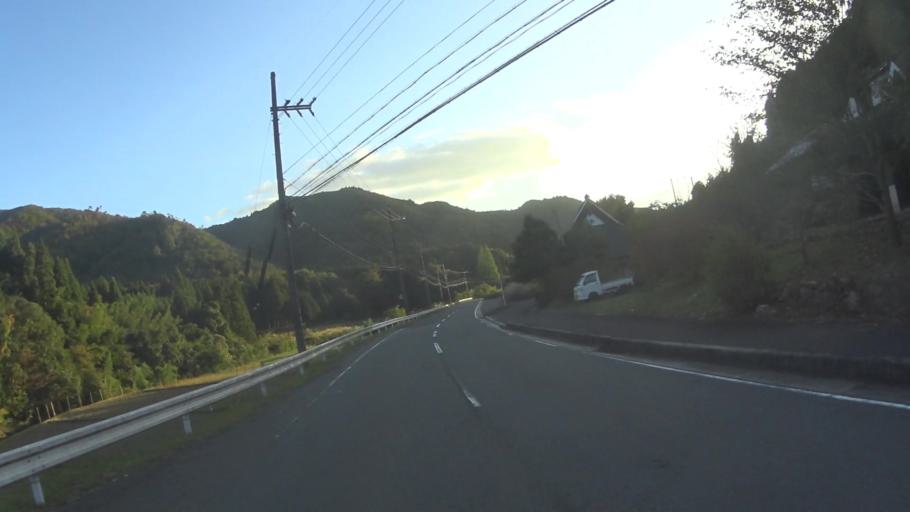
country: JP
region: Kyoto
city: Ayabe
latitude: 35.2344
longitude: 135.2545
